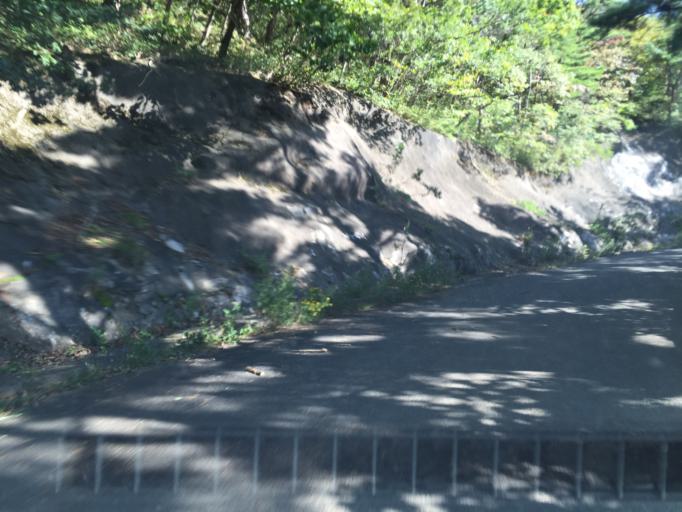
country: JP
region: Fukushima
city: Yanagawamachi-saiwaicho
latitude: 37.8461
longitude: 140.6849
